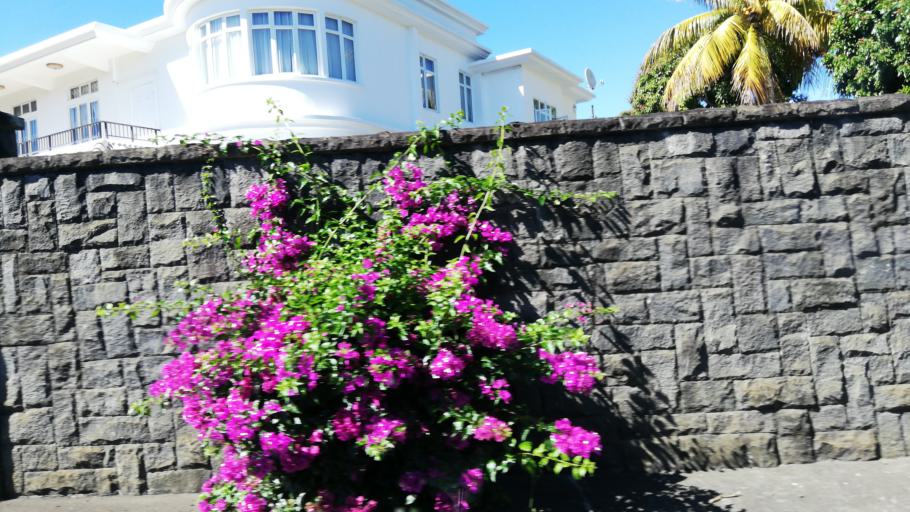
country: MU
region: Plaines Wilhems
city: Ebene
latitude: -20.2339
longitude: 57.4750
